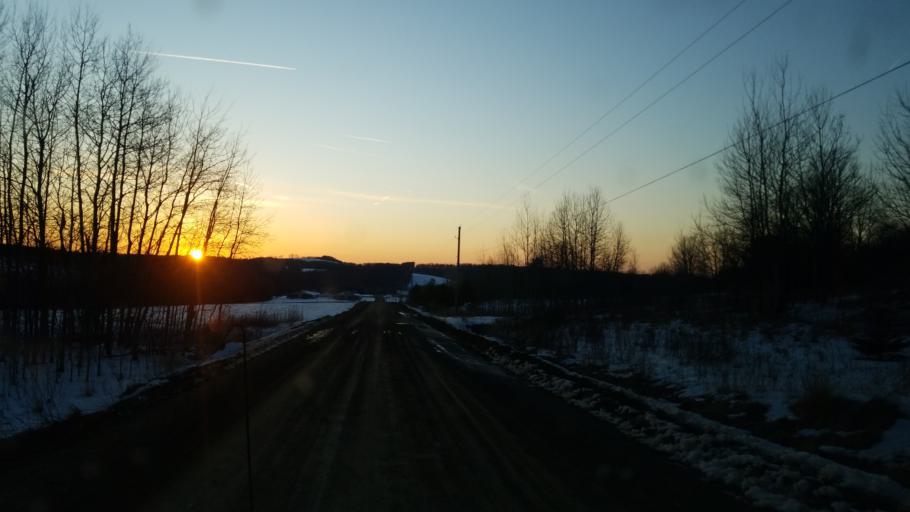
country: US
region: New York
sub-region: Allegany County
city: Andover
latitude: 42.0070
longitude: -77.7098
